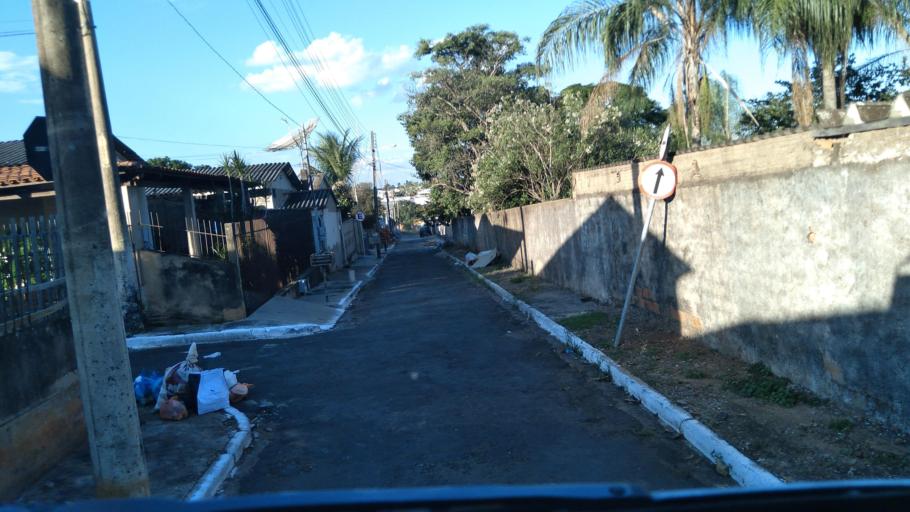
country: BR
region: Goias
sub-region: Mineiros
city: Mineiros
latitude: -17.5614
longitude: -52.5470
